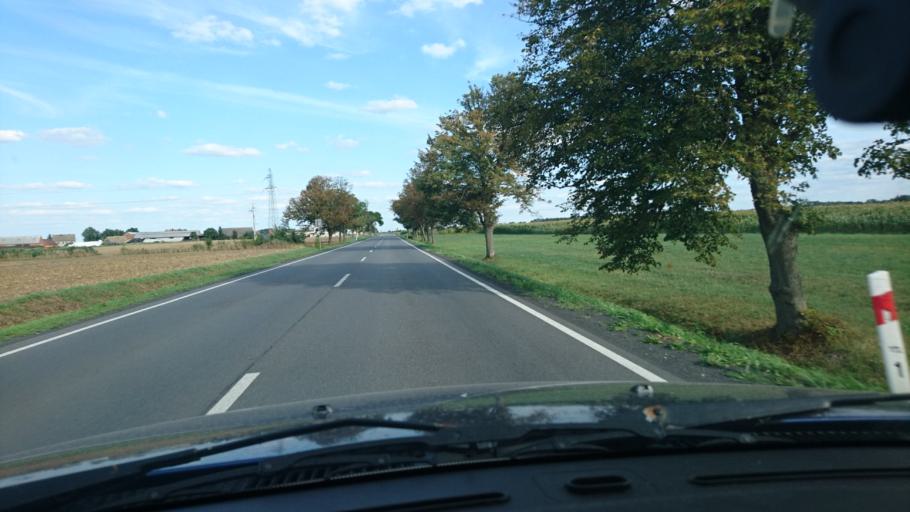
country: PL
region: Greater Poland Voivodeship
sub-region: Powiat krotoszynski
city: Zduny
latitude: 51.7232
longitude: 17.3441
